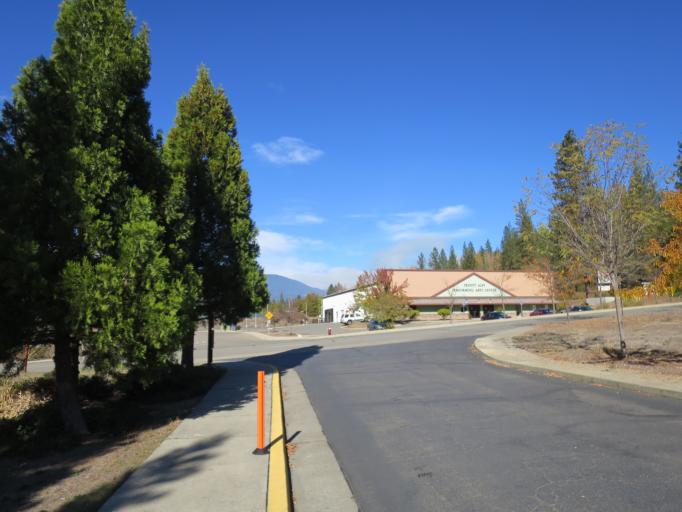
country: US
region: California
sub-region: Trinity County
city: Weaverville
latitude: 40.7100
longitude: -122.9250
